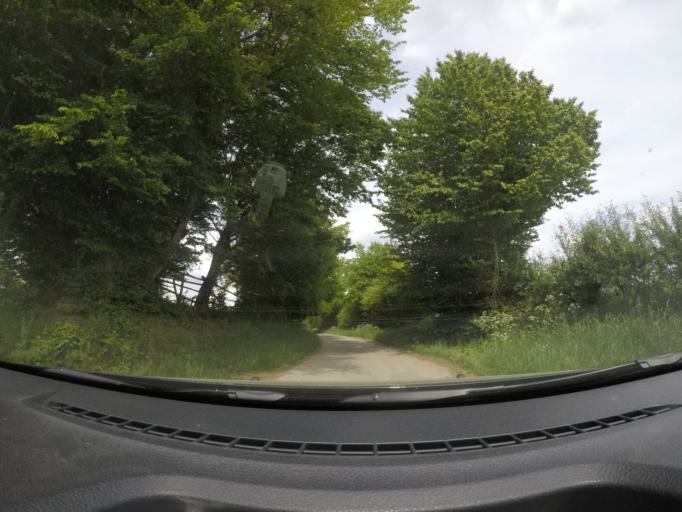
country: BE
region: Wallonia
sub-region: Province du Luxembourg
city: Leglise
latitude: 49.8155
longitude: 5.5650
